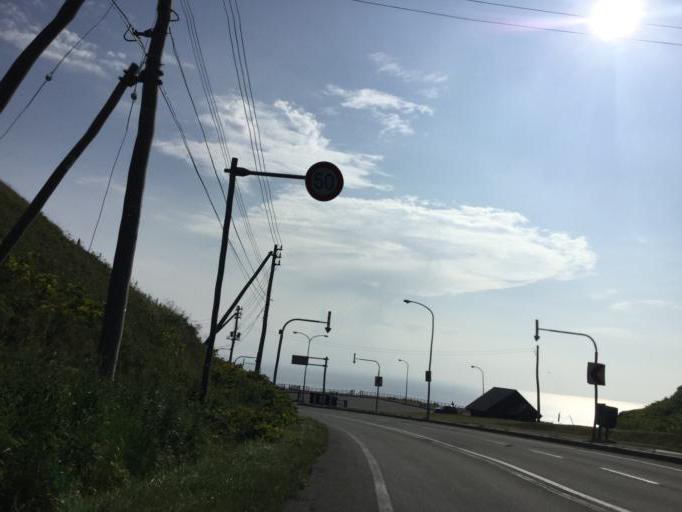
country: JP
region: Hokkaido
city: Wakkanai
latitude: 45.3807
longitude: 141.6549
